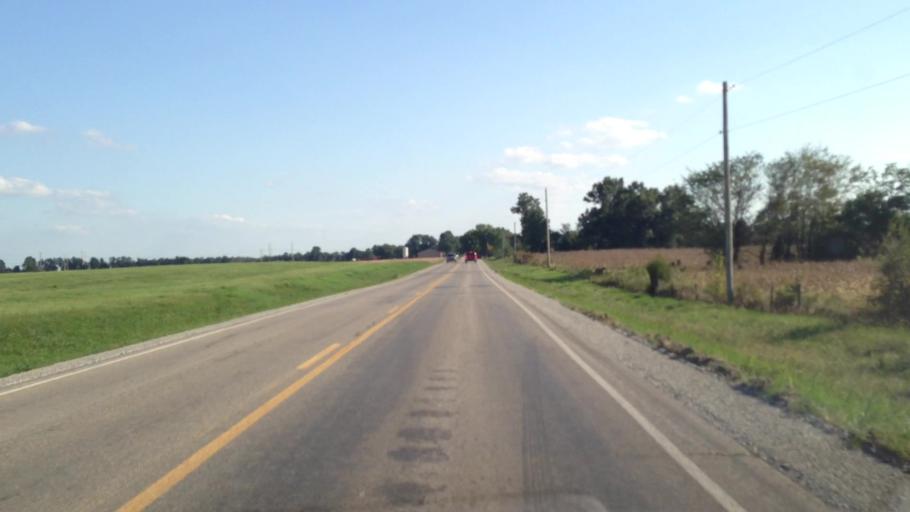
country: US
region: Kansas
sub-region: Crawford County
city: Pittsburg
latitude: 37.3417
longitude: -94.6316
